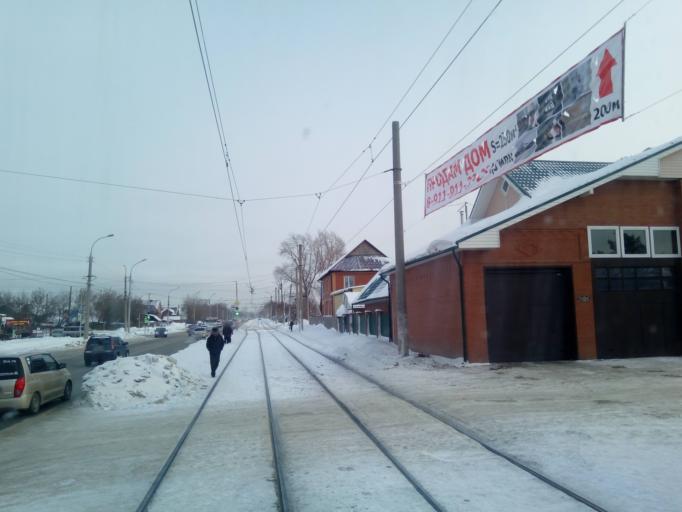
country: RU
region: Novosibirsk
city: Tolmachevo
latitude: 54.9802
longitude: 82.8338
